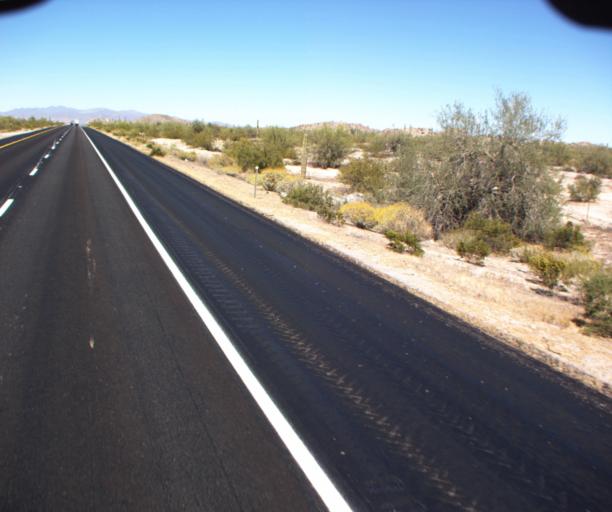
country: US
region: Arizona
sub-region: Maricopa County
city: Buckeye
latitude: 33.2861
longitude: -112.6296
